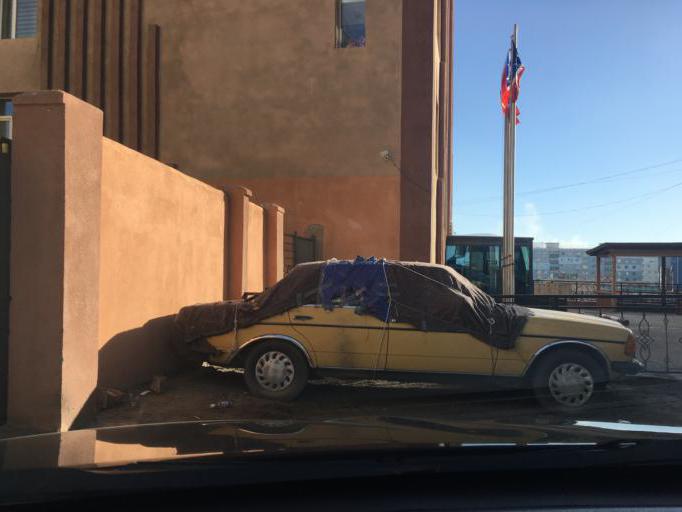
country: MN
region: Ulaanbaatar
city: Ulaanbaatar
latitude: 47.9244
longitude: 106.8746
